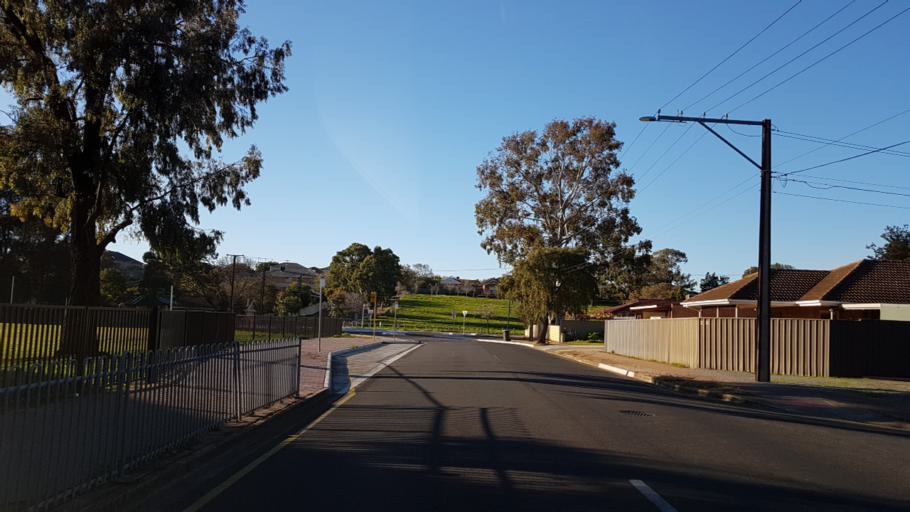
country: AU
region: South Australia
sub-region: Campbelltown
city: Hectorville
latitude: -34.8824
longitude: 138.6547
